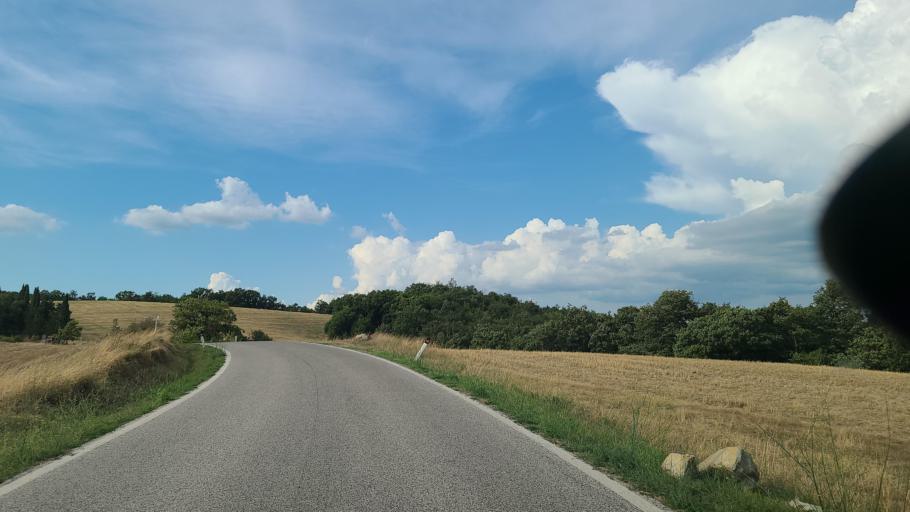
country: IT
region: Tuscany
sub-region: Provincia di Siena
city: San Gimignano
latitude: 43.4263
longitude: 10.9738
